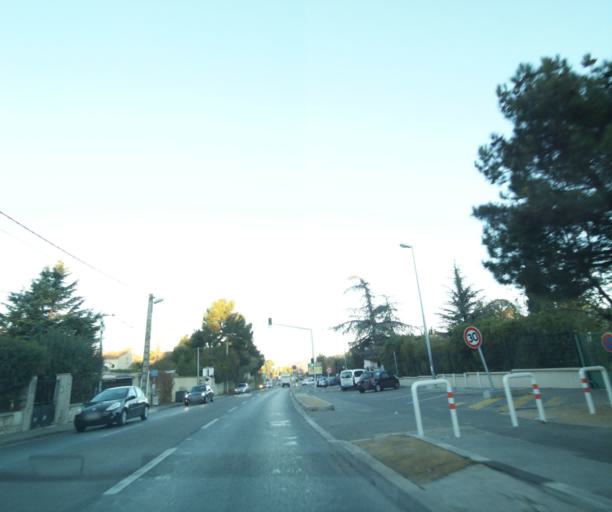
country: FR
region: Provence-Alpes-Cote d'Azur
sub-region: Departement des Bouches-du-Rhone
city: Allauch
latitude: 43.3141
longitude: 5.4628
